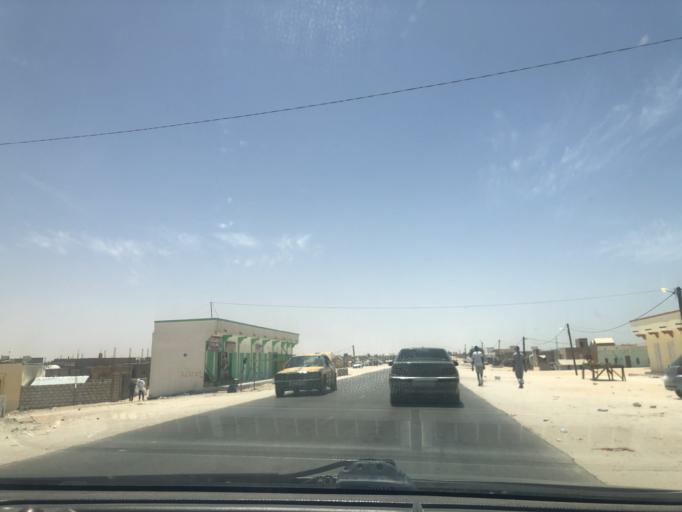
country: MR
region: Nouakchott
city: Nouakchott
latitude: 18.0138
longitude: -15.9591
